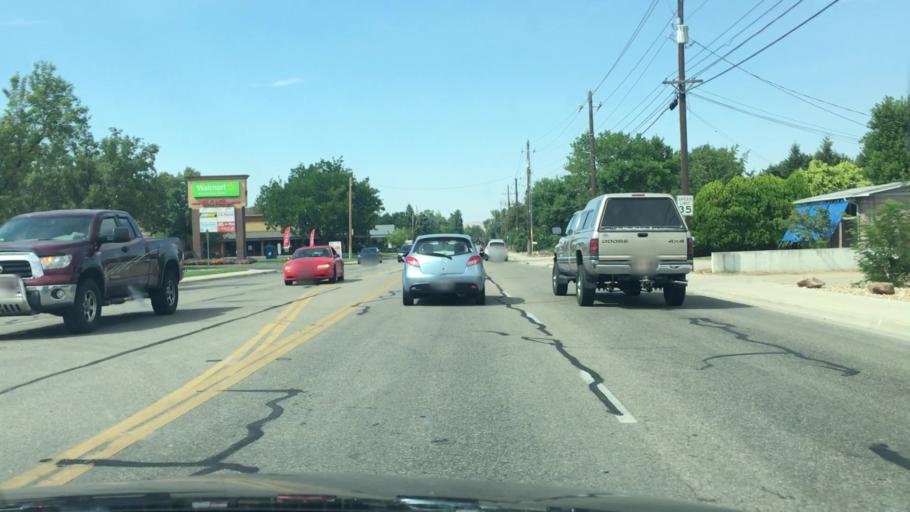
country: US
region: Idaho
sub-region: Ada County
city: Garden City
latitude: 43.6347
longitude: -116.2742
